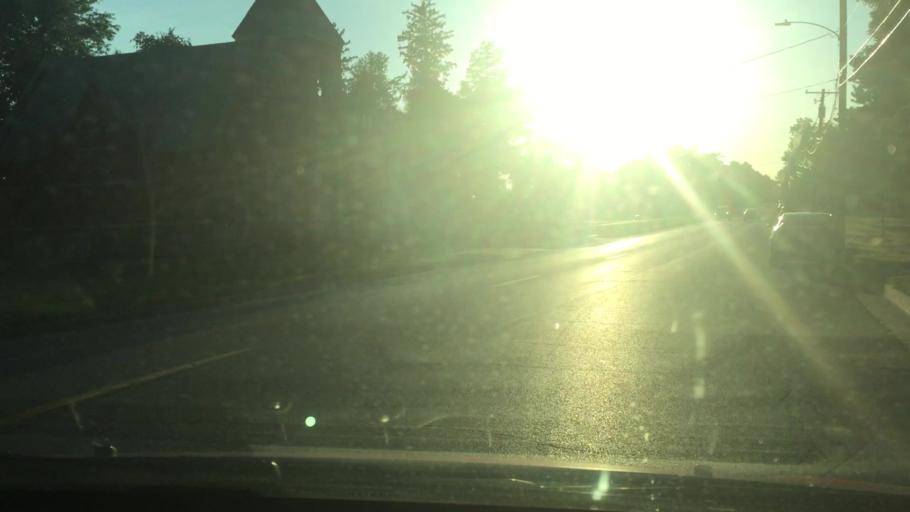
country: US
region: Iowa
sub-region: Muscatine County
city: Muscatine
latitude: 41.4199
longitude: -91.0636
